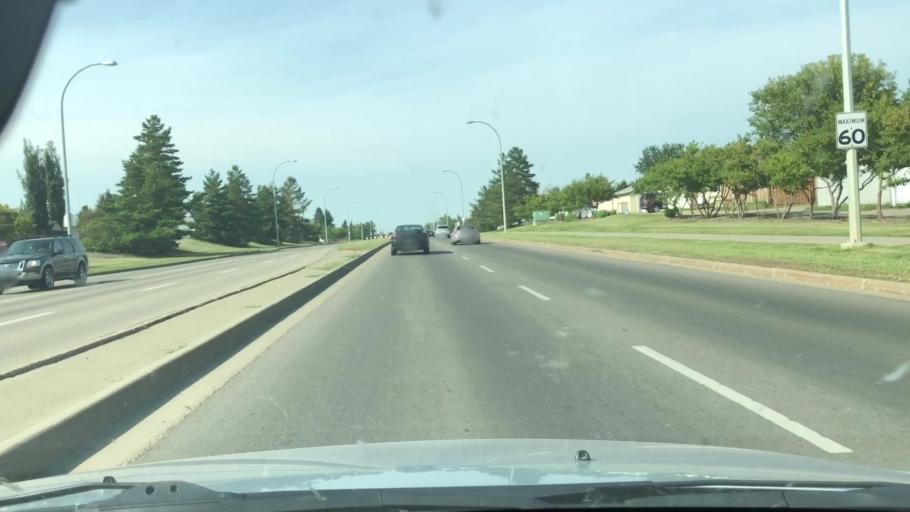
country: CA
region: Alberta
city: Edmonton
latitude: 53.6104
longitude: -113.4428
